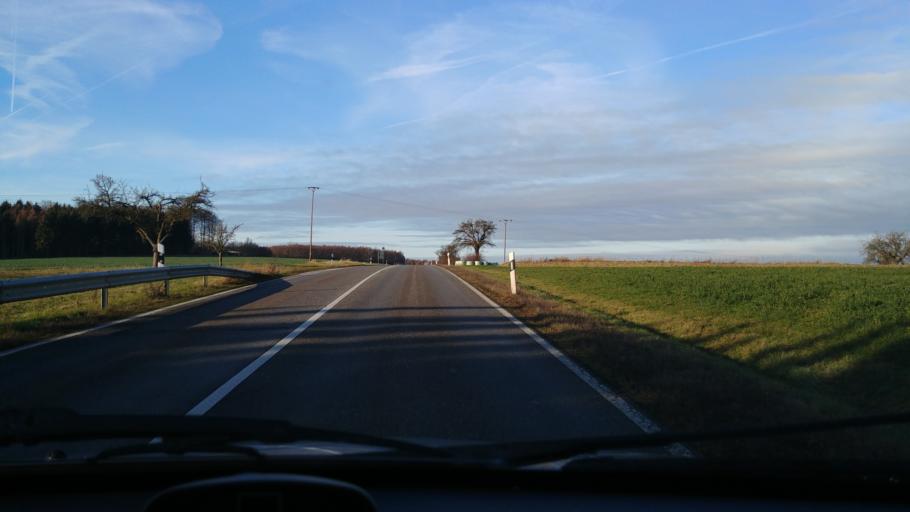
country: DE
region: Rheinland-Pfalz
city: Pohl
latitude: 50.2514
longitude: 7.8648
